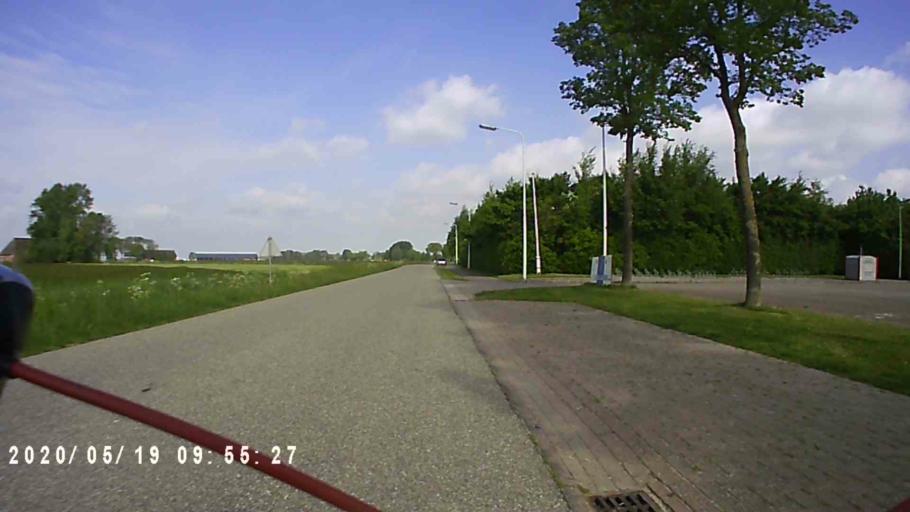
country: NL
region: Groningen
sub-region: Gemeente Zuidhorn
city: Grijpskerk
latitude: 53.2908
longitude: 6.2470
